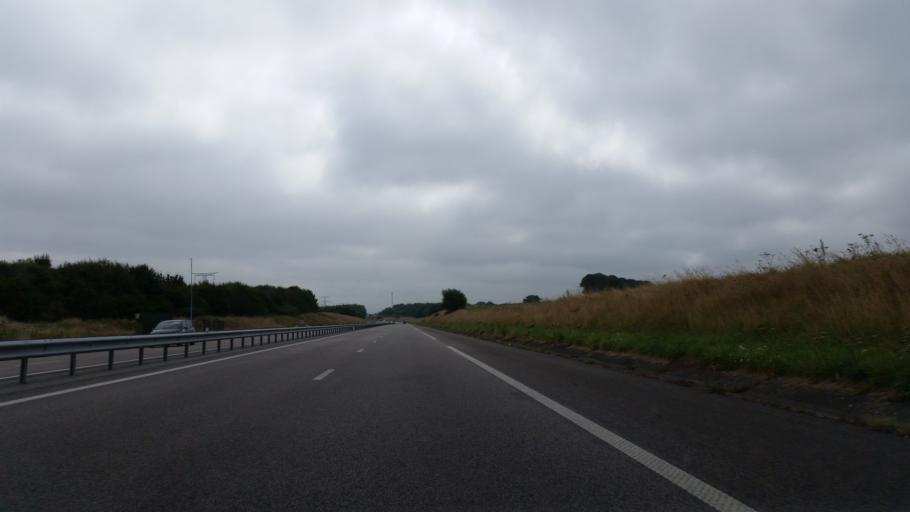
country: FR
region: Haute-Normandie
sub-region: Departement de la Seine-Maritime
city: Cleres
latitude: 49.6341
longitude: 1.1067
